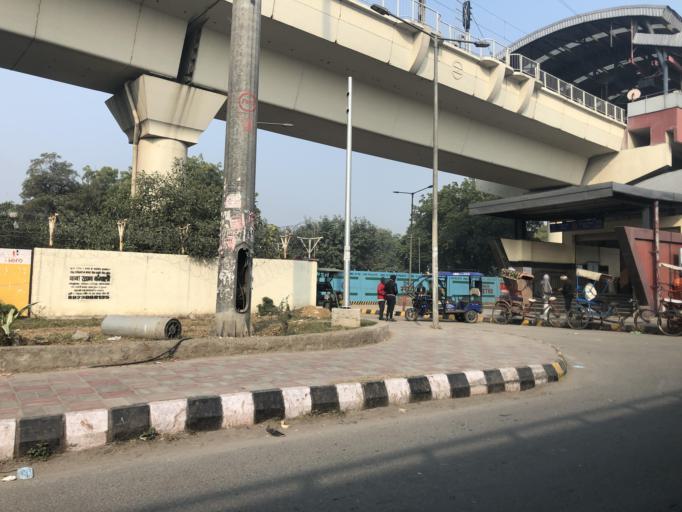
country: IN
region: NCT
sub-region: North West Delhi
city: Pitampura
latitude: 28.6718
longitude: 77.1391
